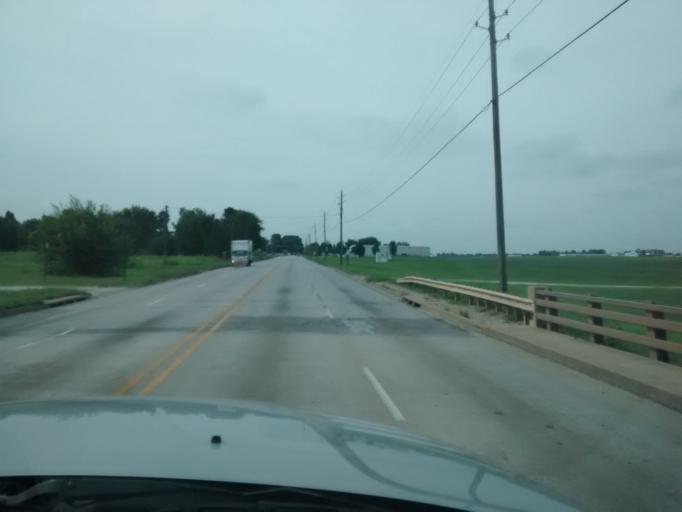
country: US
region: Arkansas
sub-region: Washington County
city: Springdale
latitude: 36.1811
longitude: -94.1163
